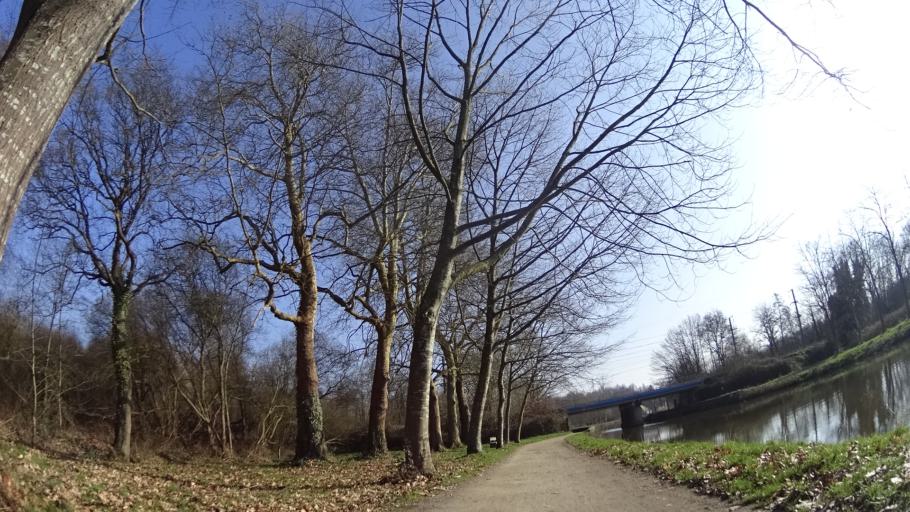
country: FR
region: Brittany
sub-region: Departement d'Ille-et-Vilaine
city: Saint-Gregoire
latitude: 48.1437
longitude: -1.6763
